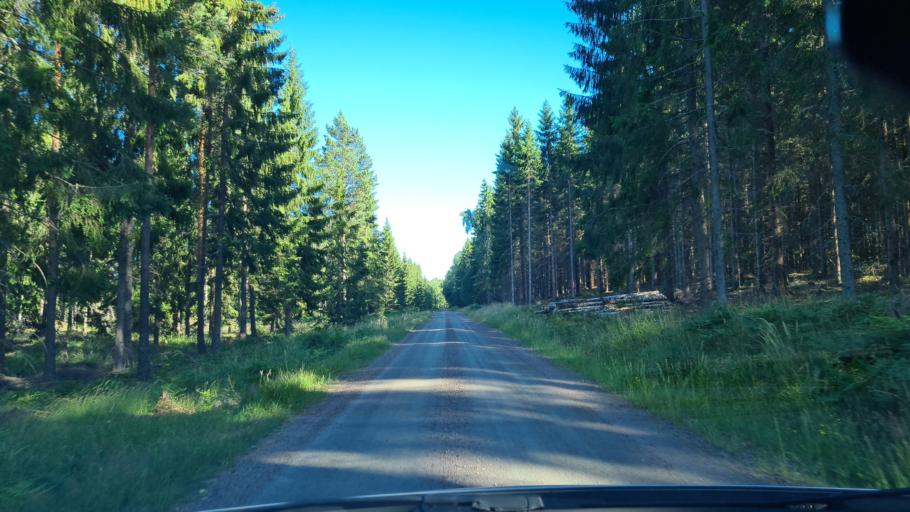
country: SE
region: Soedermanland
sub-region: Nykopings Kommun
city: Stigtomta
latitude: 58.9227
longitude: 16.9057
